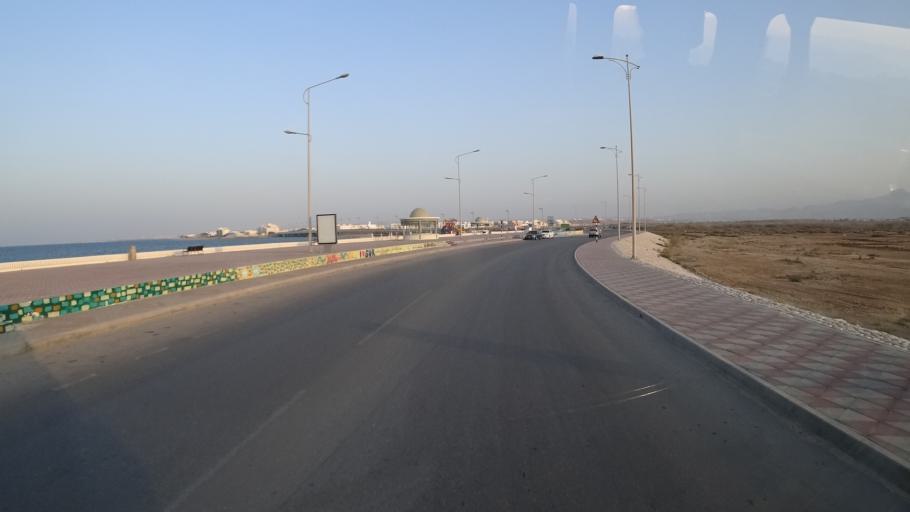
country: OM
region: Ash Sharqiyah
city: Sur
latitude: 22.6014
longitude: 59.4851
